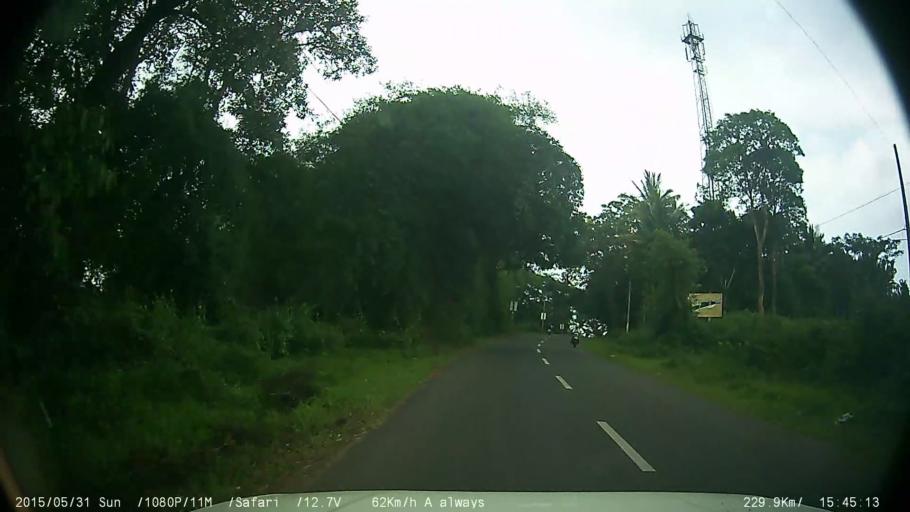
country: IN
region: Kerala
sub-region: Wayanad
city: Panamaram
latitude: 11.6750
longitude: 76.2939
